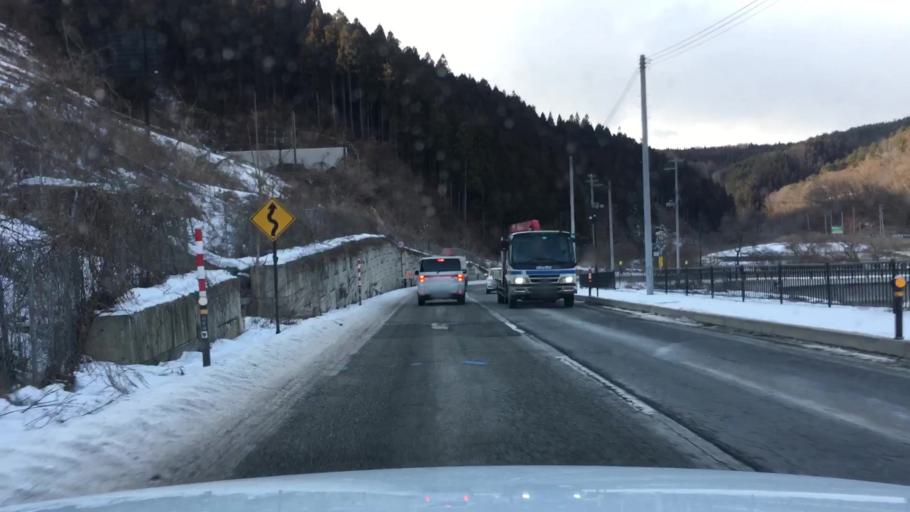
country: JP
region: Iwate
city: Morioka-shi
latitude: 39.6724
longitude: 141.2298
